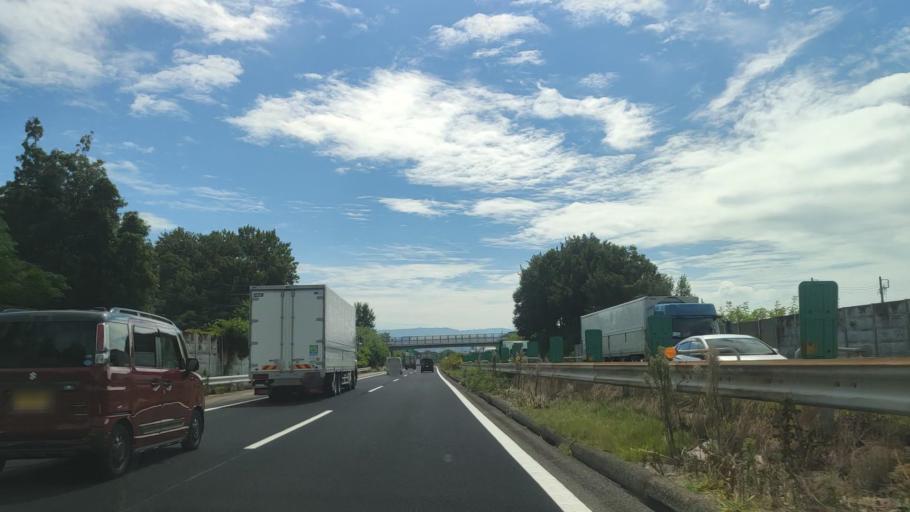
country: JP
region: Aichi
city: Okazaki
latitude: 34.9494
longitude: 137.1972
